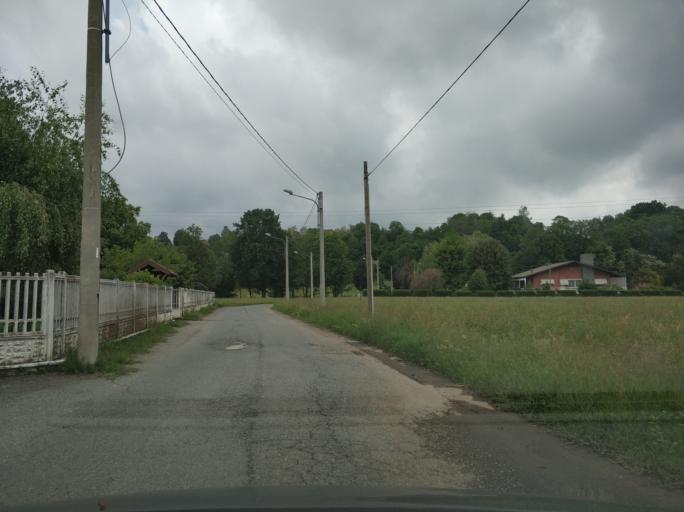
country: IT
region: Piedmont
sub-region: Provincia di Torino
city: Nole
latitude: 45.2495
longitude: 7.5871
